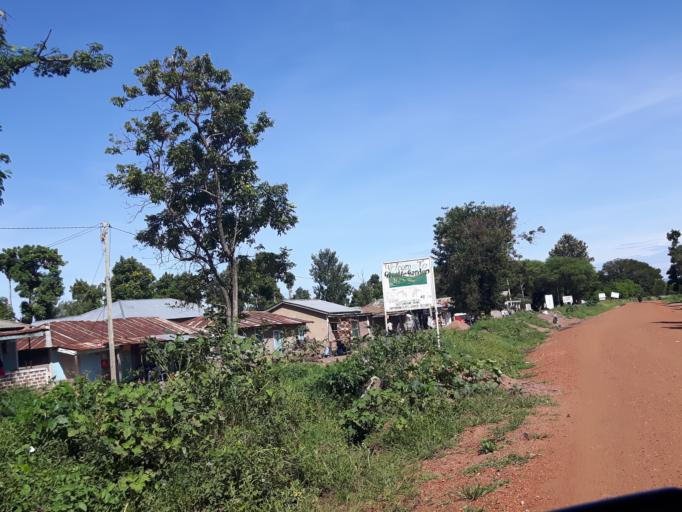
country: TZ
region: Mara
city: Issenye
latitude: -1.9895
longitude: 34.3491
